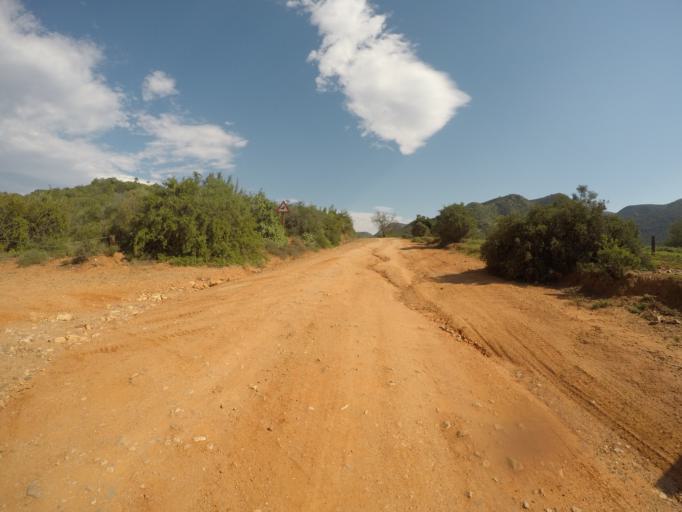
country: ZA
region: Eastern Cape
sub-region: Cacadu District Municipality
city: Kareedouw
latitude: -33.6545
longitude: 24.4129
